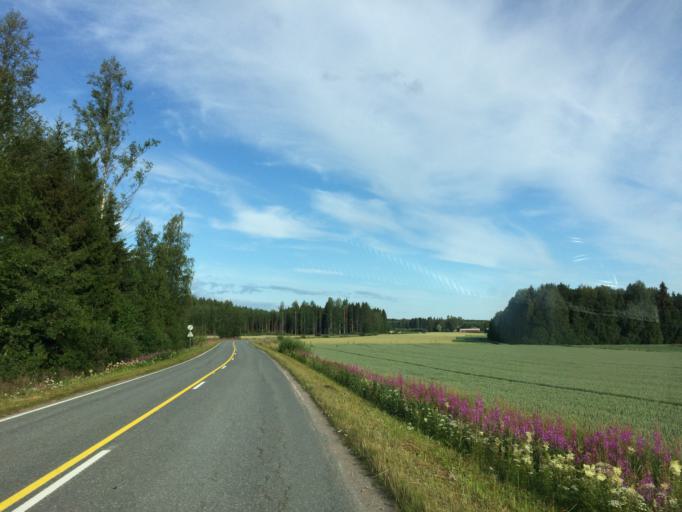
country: FI
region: Haeme
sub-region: Haemeenlinna
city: Janakkala
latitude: 60.9306
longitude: 24.5519
